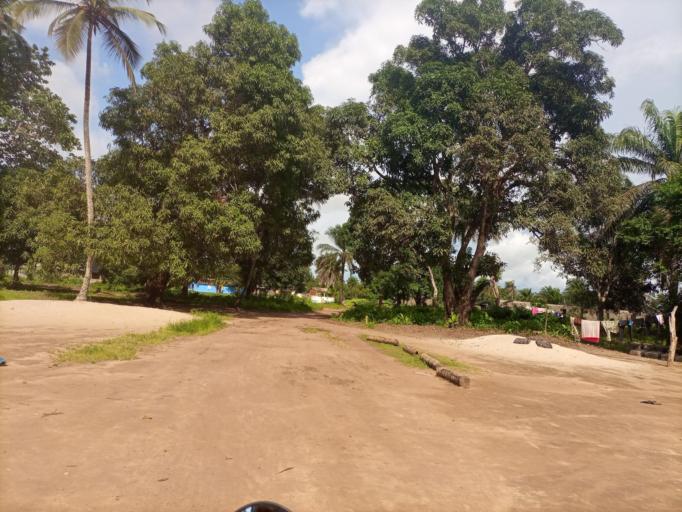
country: SL
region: Northern Province
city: Sawkta
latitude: 8.6296
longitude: -13.1832
